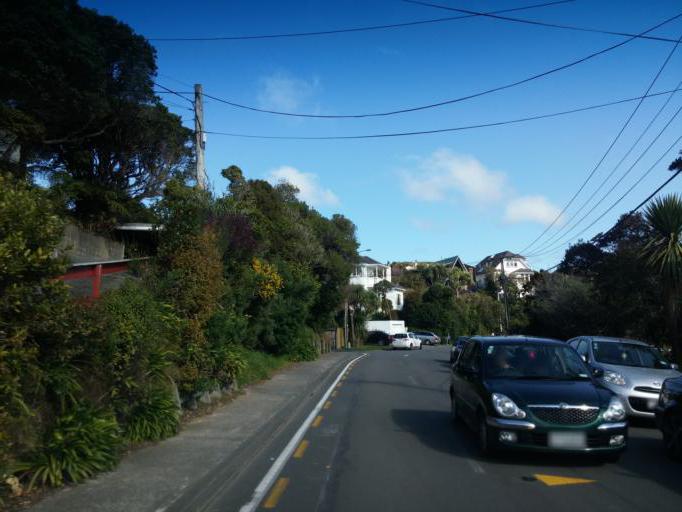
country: NZ
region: Wellington
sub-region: Wellington City
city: Wellington
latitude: -41.2485
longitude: 174.7890
